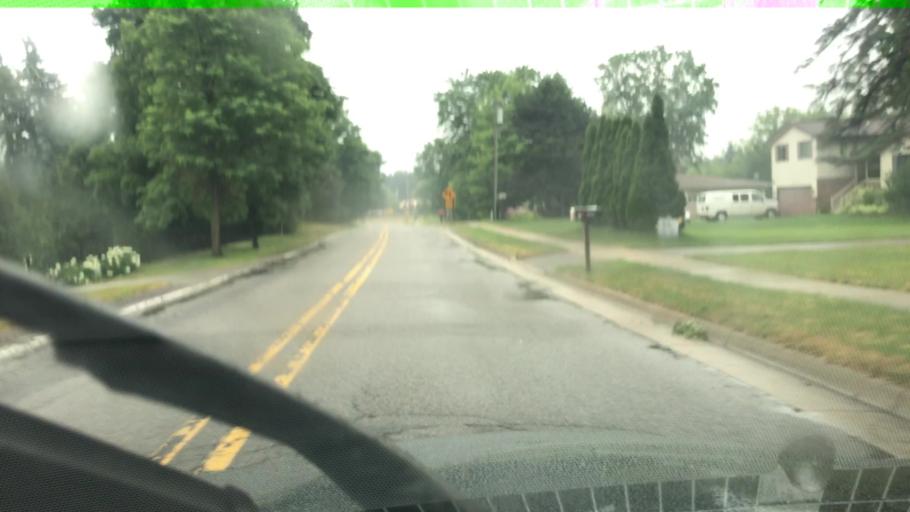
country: US
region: Michigan
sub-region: Oakland County
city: Auburn Hills
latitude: 42.7244
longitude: -83.2724
